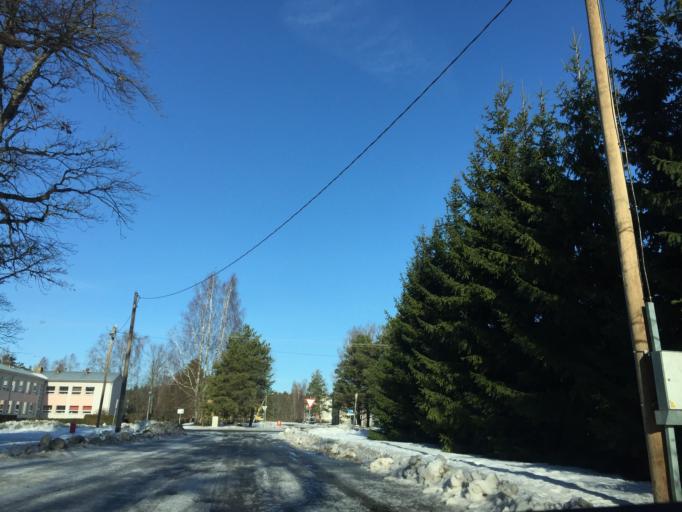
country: EE
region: Paernumaa
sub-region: Paikuse vald
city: Paikuse
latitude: 58.2796
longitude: 24.5776
